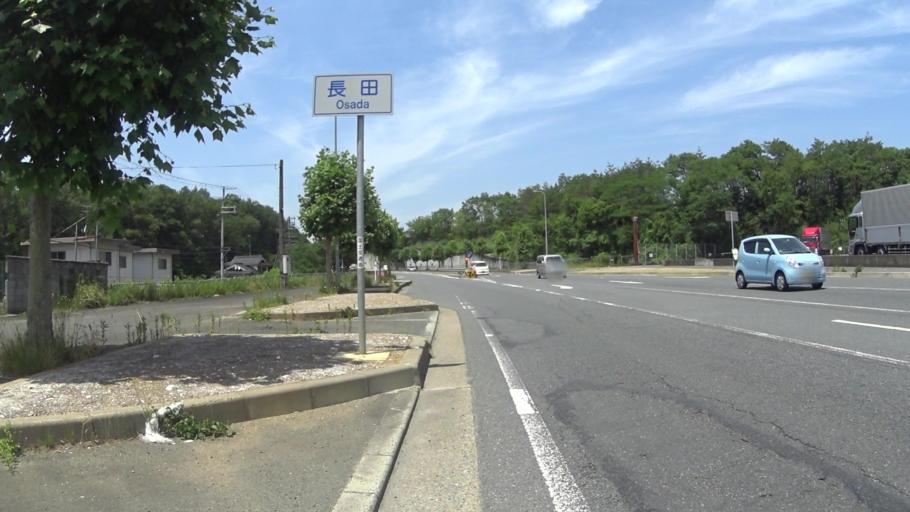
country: JP
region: Kyoto
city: Ayabe
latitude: 35.2736
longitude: 135.1834
